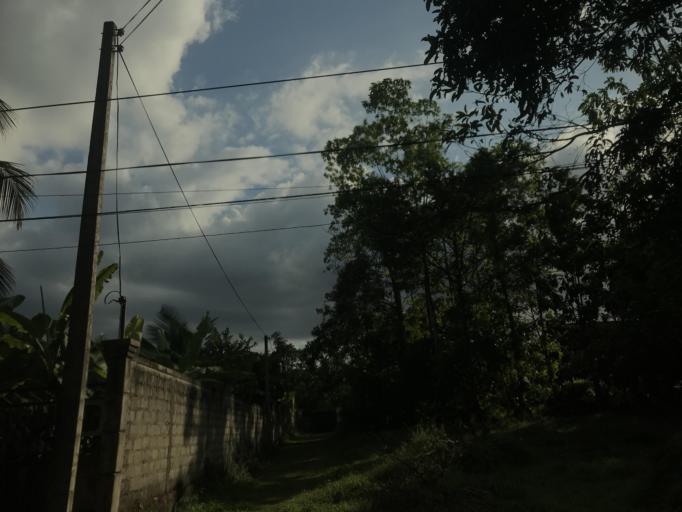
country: LK
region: Western
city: Gampaha
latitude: 7.0654
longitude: 80.0061
